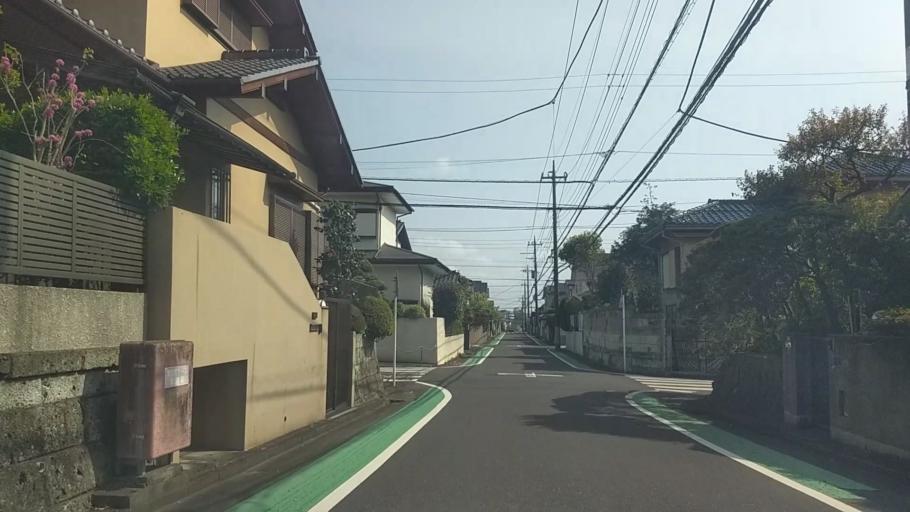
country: JP
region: Kanagawa
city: Kamakura
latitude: 35.3808
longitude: 139.5660
